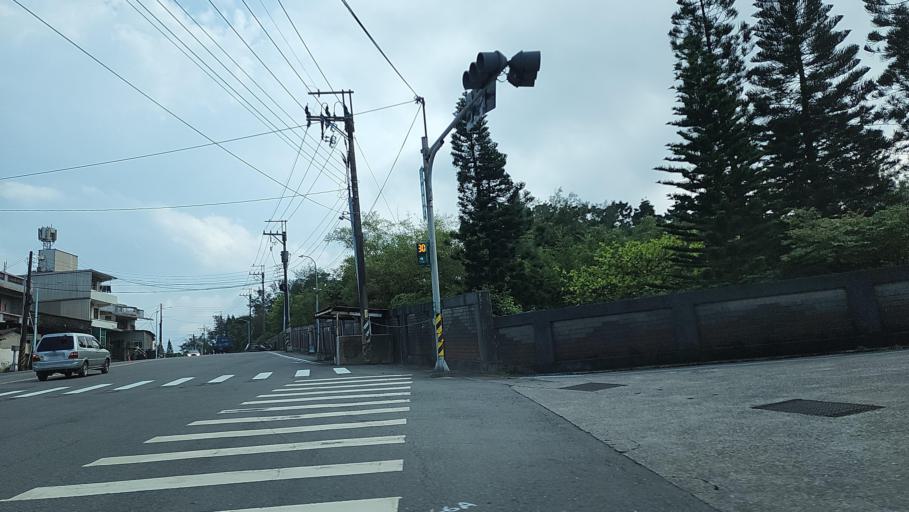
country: TW
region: Taiwan
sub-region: Keelung
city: Keelung
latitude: 25.2272
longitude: 121.6437
